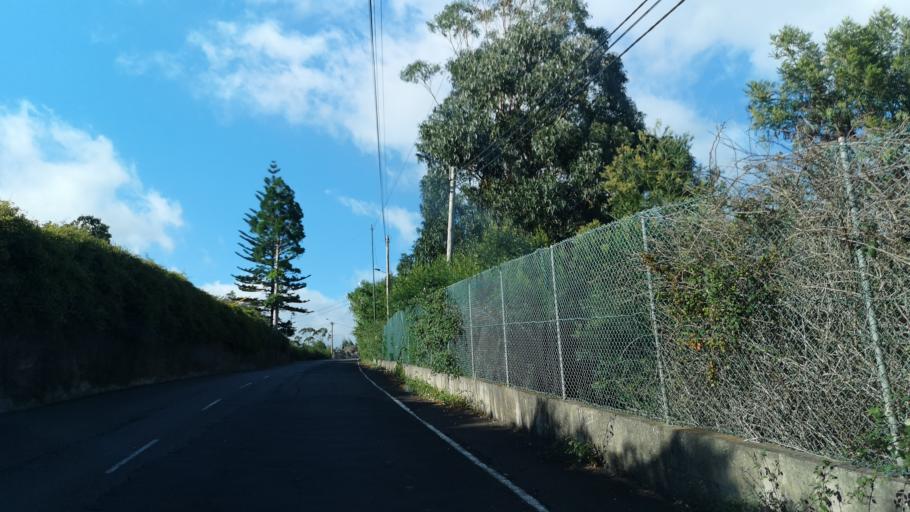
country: PT
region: Madeira
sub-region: Santa Cruz
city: Camacha
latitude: 32.6609
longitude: -16.8361
